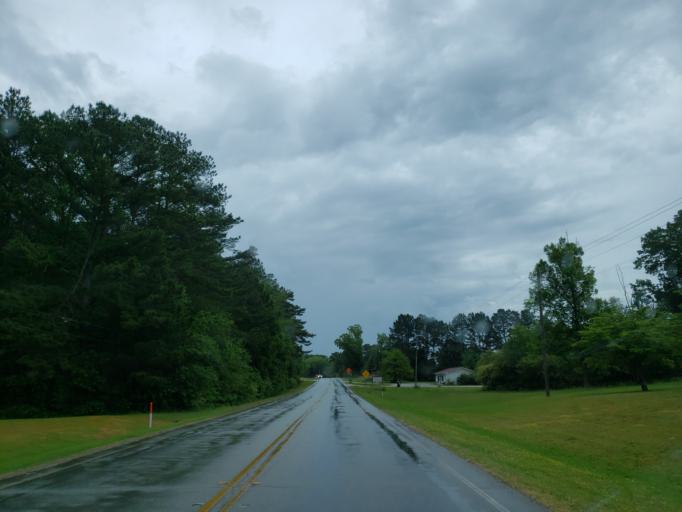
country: US
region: Georgia
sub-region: Haralson County
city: Buchanan
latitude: 33.7921
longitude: -85.1830
